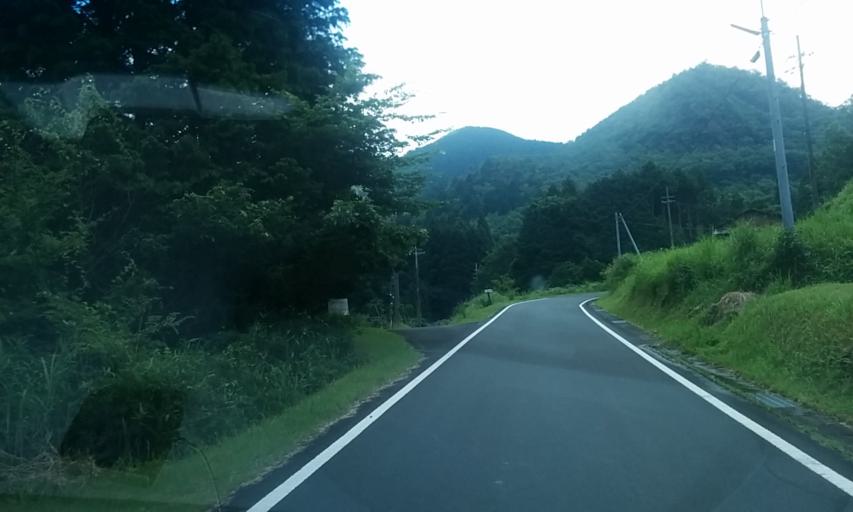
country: JP
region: Kyoto
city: Ayabe
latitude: 35.1884
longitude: 135.2172
